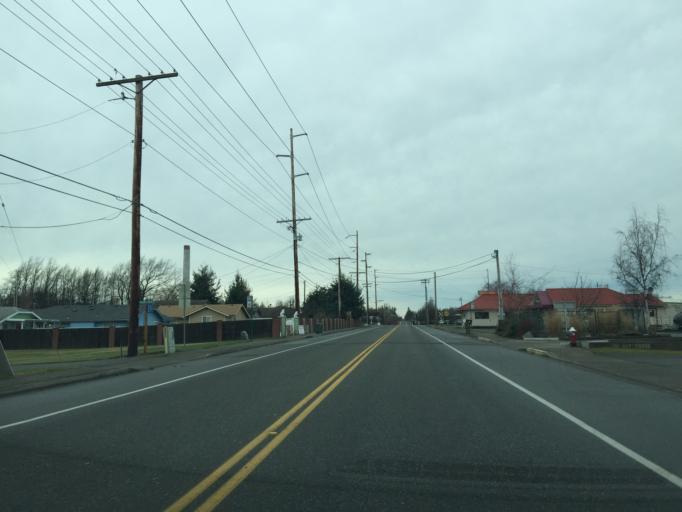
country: US
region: Washington
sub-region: Whatcom County
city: Bellingham
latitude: 48.7673
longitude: -122.5177
